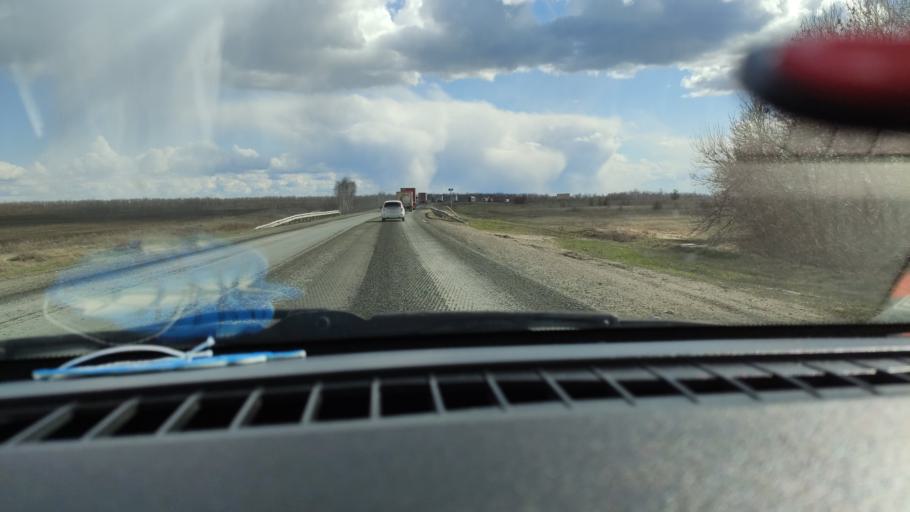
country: RU
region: Saratov
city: Dukhovnitskoye
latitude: 52.7147
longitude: 48.2667
